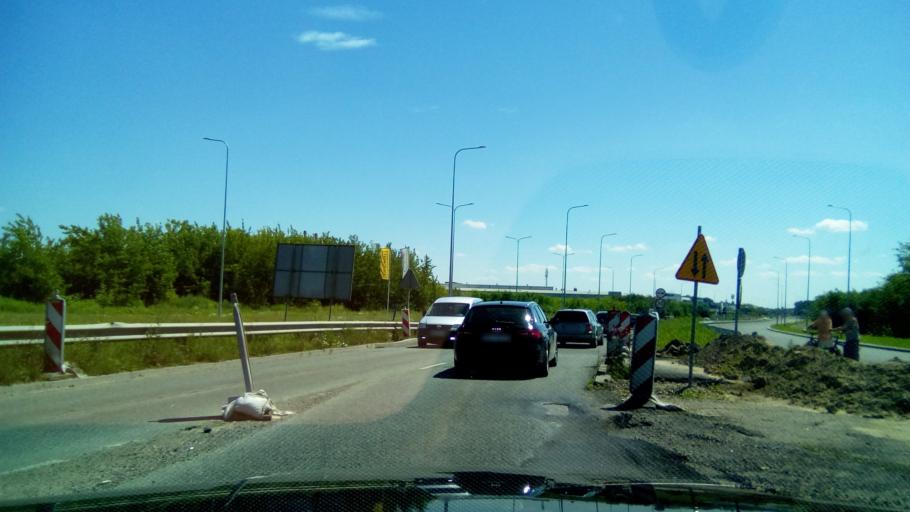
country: PL
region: Masovian Voivodeship
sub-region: Radom
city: Radom
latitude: 51.4188
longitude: 21.1898
